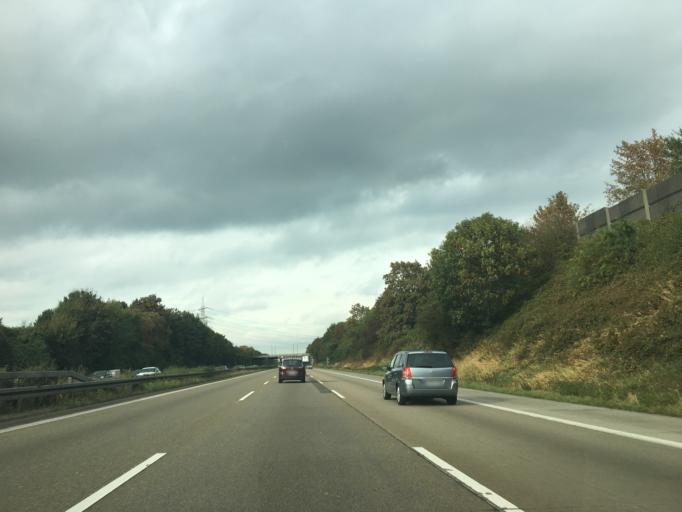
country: DE
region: North Rhine-Westphalia
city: Opladen
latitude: 51.0739
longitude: 6.9881
